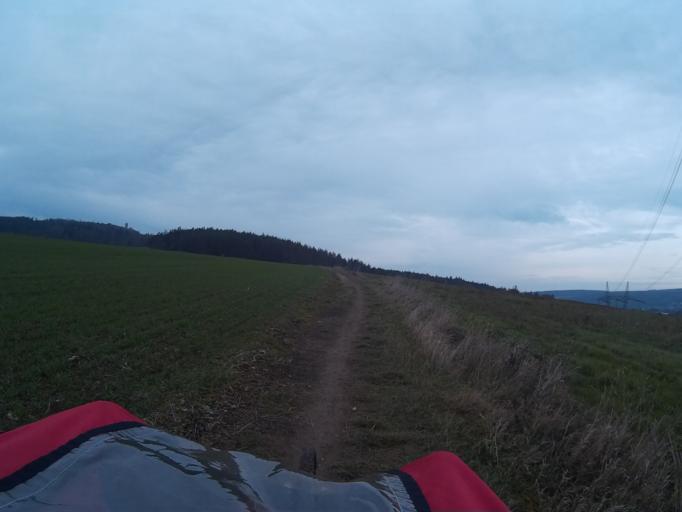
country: CZ
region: Plzensky
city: St'ahlavy
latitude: 49.6792
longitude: 13.4871
